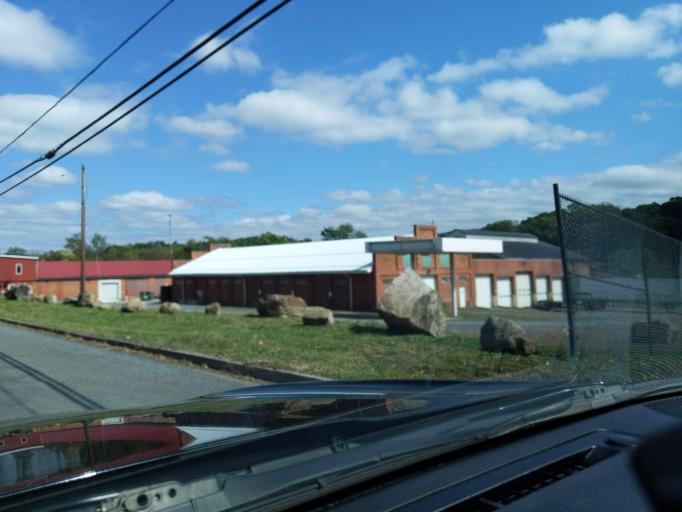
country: US
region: Pennsylvania
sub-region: Blair County
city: Lakemont
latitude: 40.4888
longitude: -78.4198
